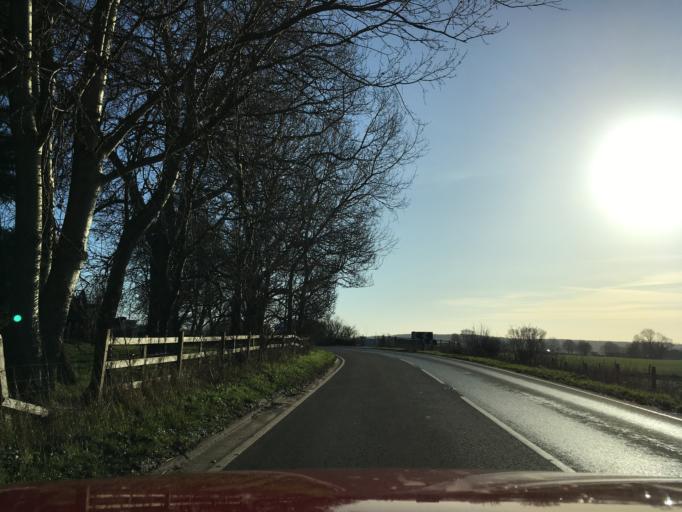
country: GB
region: England
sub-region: Warwickshire
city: Wellesbourne Mountford
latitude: 52.1995
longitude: -1.6215
